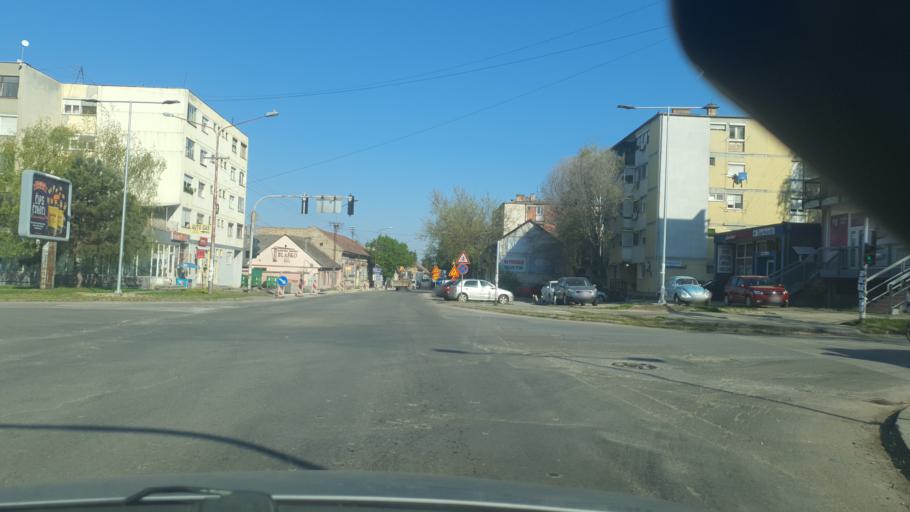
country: RS
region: Autonomna Pokrajina Vojvodina
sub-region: Zapadnobacki Okrug
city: Kula
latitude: 45.6126
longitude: 19.5277
